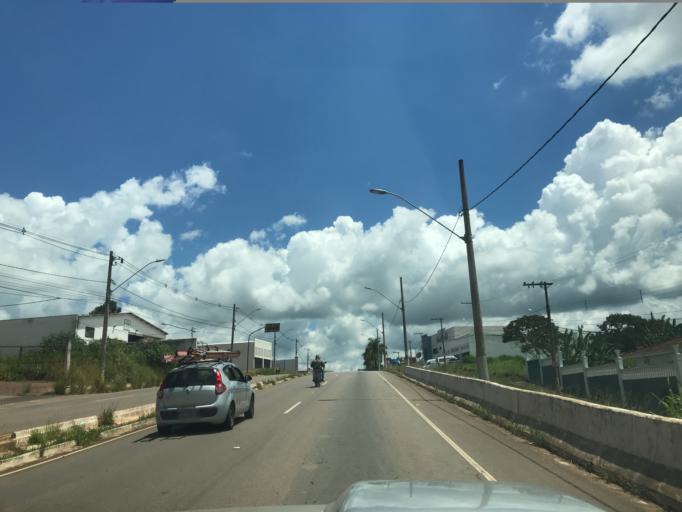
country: BR
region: Minas Gerais
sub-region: Tres Coracoes
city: Tres Coracoes
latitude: -21.6715
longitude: -45.2725
